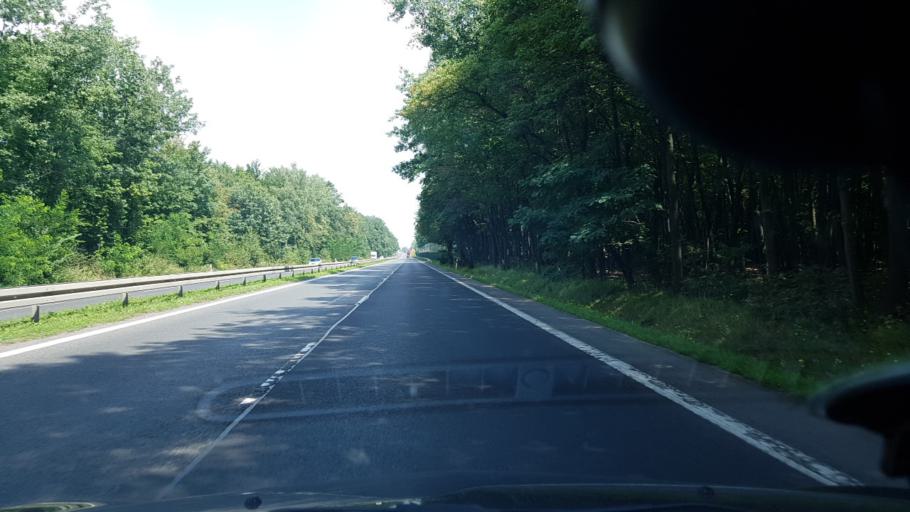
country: PL
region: Silesian Voivodeship
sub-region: Powiat mikolowski
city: Mikolow
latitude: 50.2049
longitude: 18.9526
